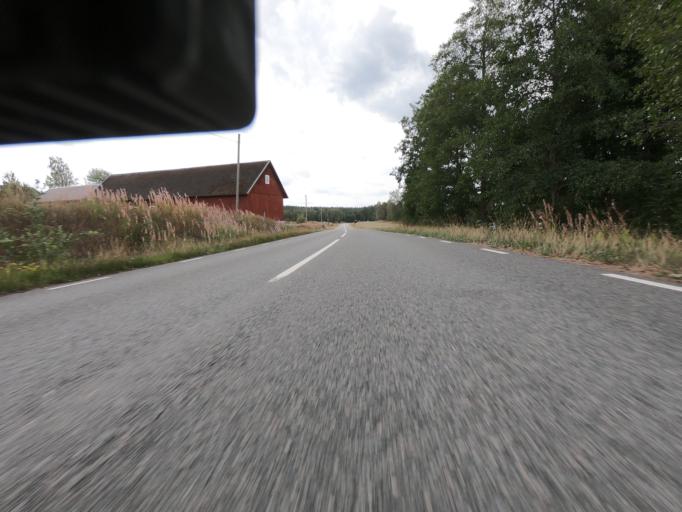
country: SE
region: Joenkoeping
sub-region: Vetlanda Kommun
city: Landsbro
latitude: 57.2225
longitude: 14.9498
